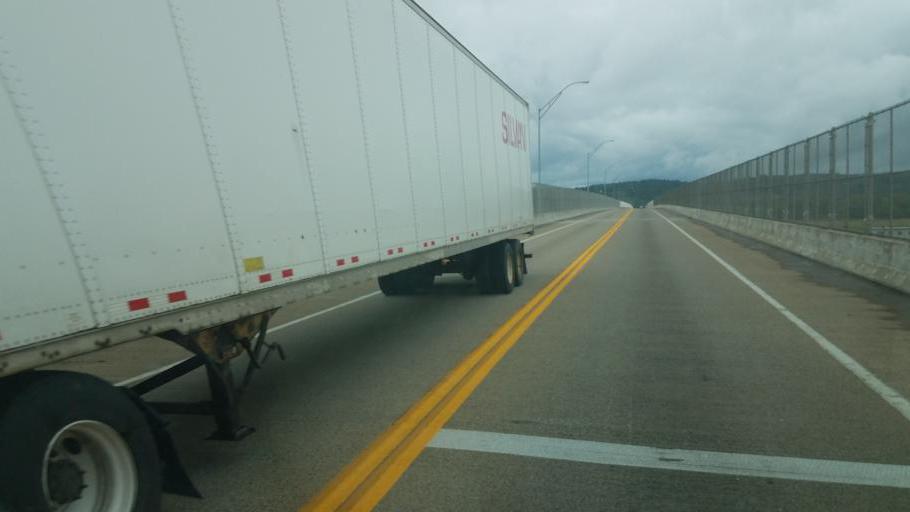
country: US
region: Ohio
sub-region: Scioto County
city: Franklin Furnace
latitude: 38.6471
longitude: -82.8573
